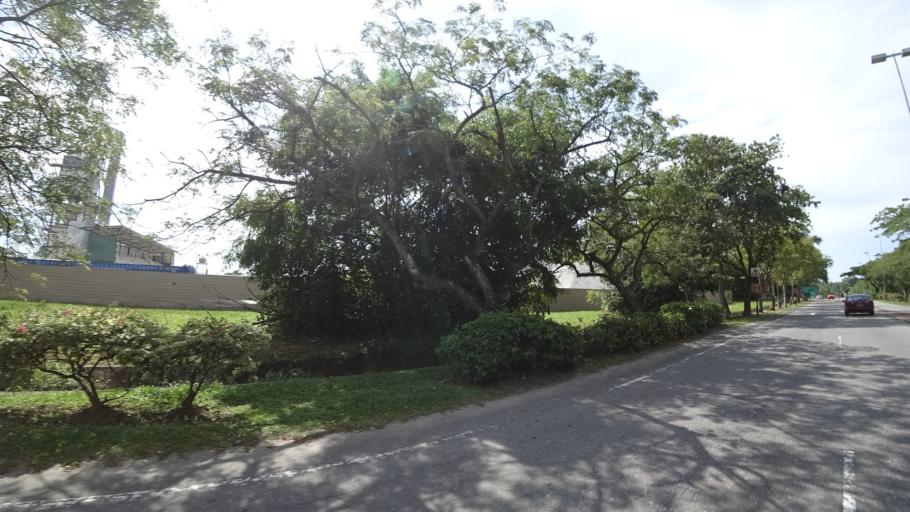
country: BN
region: Brunei and Muara
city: Bandar Seri Begawan
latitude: 4.9404
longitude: 114.9354
